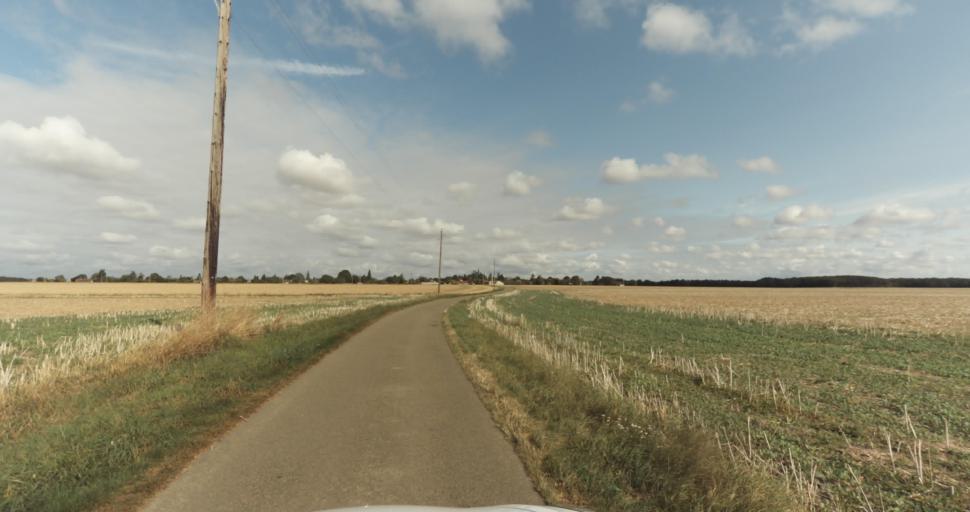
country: FR
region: Haute-Normandie
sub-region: Departement de l'Eure
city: Tillieres-sur-Avre
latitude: 48.7512
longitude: 1.1132
